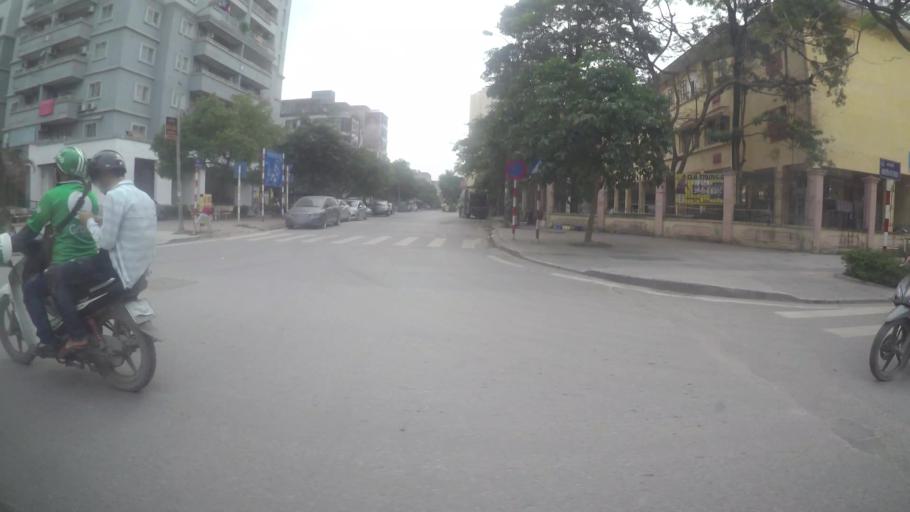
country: VN
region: Ha Noi
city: Cau Dien
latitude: 21.0366
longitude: 105.7666
